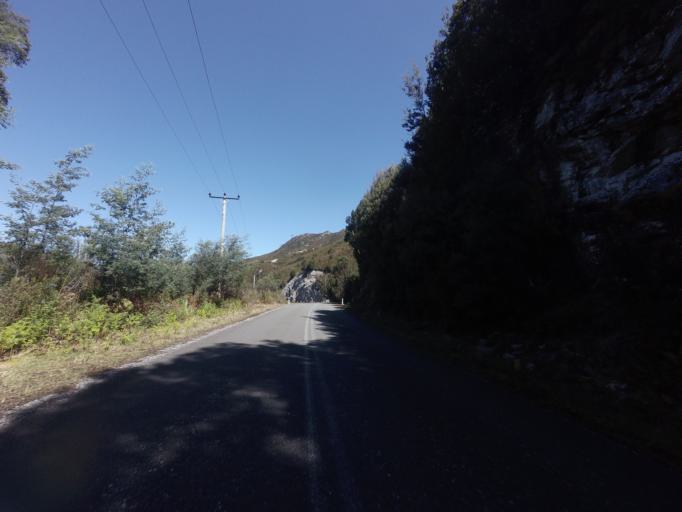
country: AU
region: Tasmania
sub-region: West Coast
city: Queenstown
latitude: -42.7440
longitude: 145.9807
